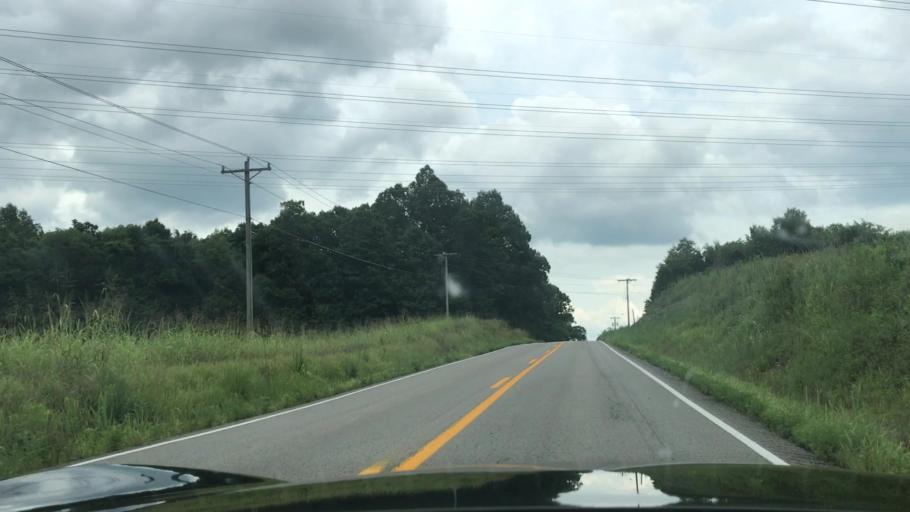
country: US
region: Kentucky
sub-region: Muhlenberg County
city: Central City
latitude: 37.1987
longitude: -87.0007
